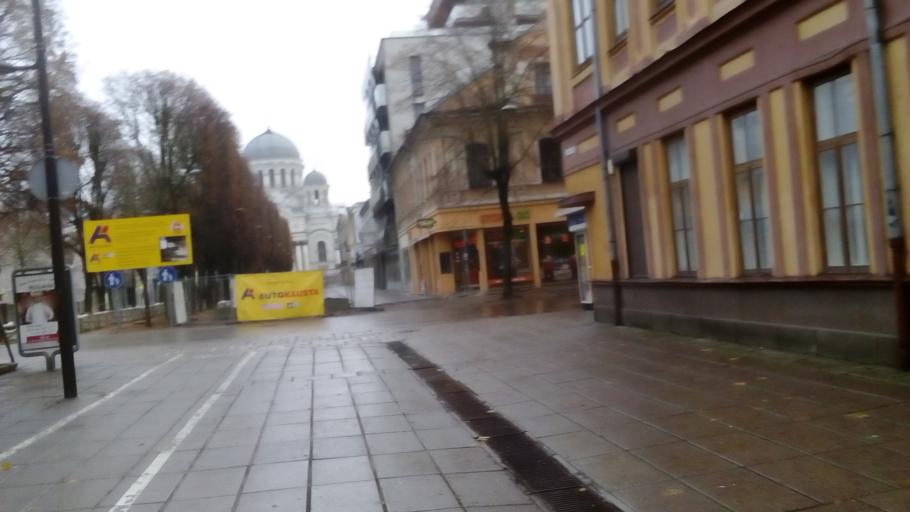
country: LT
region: Kauno apskritis
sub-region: Kaunas
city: Kaunas
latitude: 54.8961
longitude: 23.9172
